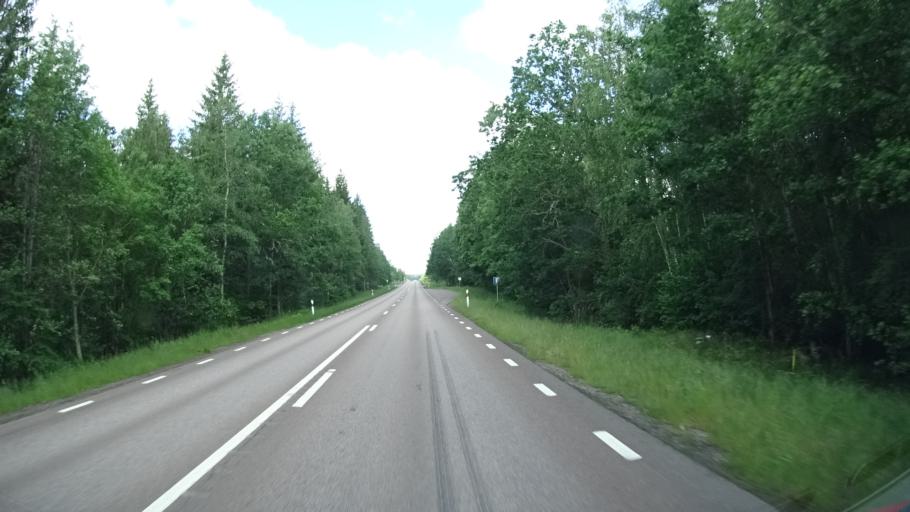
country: SE
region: Kalmar
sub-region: Hogsby Kommun
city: Hoegsby
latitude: 57.1507
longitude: 15.9411
